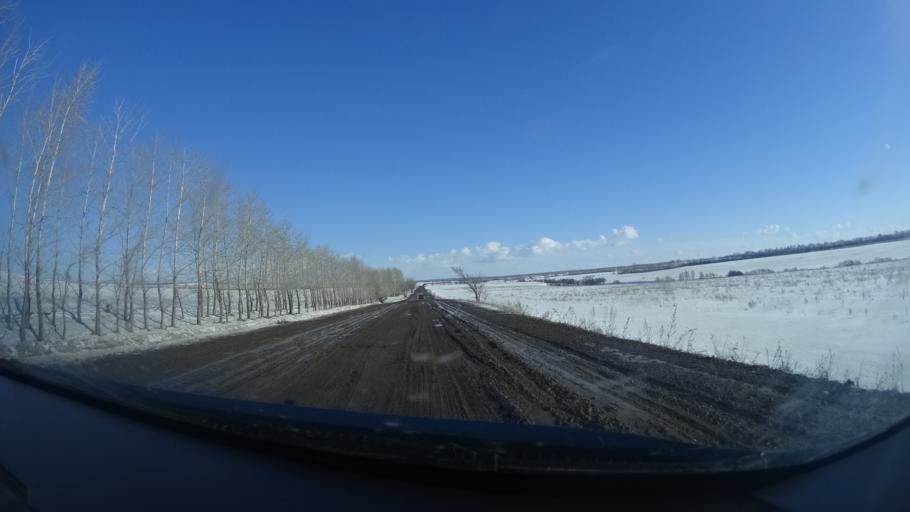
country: RU
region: Bashkortostan
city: Chishmy
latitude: 54.6019
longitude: 55.2192
